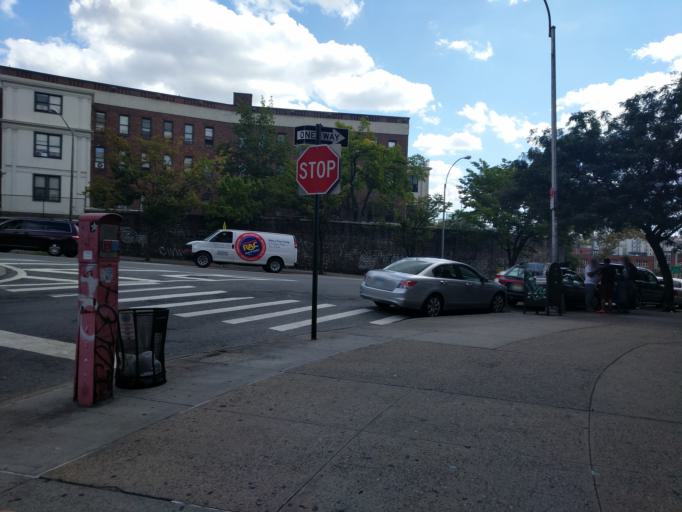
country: US
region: New York
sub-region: New York County
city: Inwood
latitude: 40.8462
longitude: -73.9175
